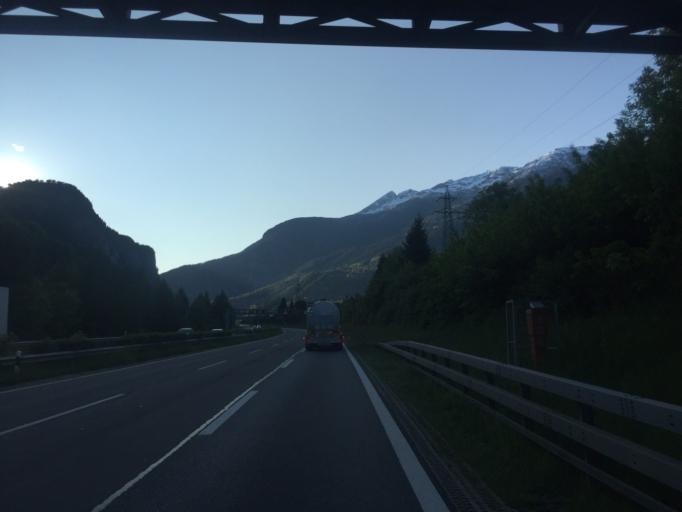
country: CH
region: Ticino
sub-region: Leventina District
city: Faido
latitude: 46.4708
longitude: 8.8112
